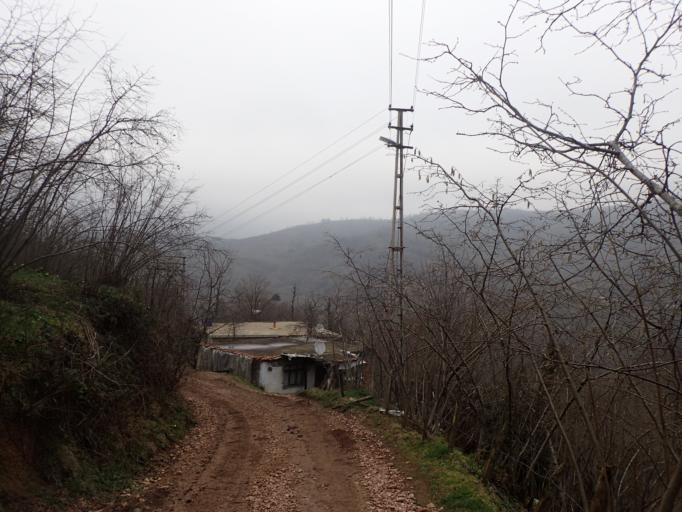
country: TR
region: Ordu
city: Camas
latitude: 40.9214
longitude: 37.5639
